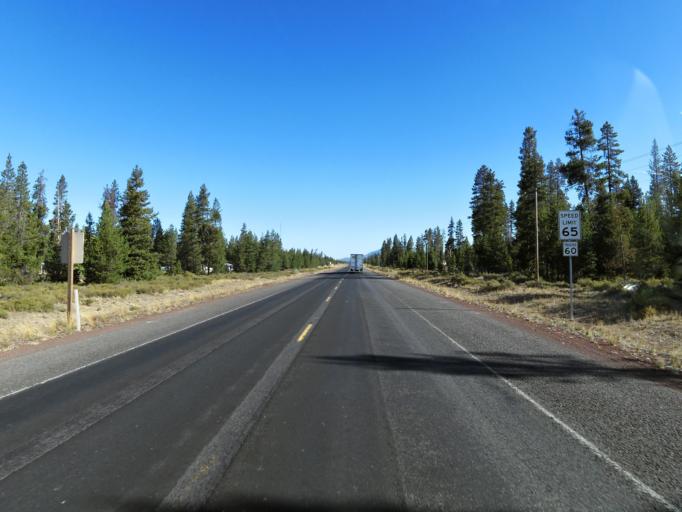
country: US
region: Oregon
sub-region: Deschutes County
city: La Pine
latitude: 43.1364
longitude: -121.8020
